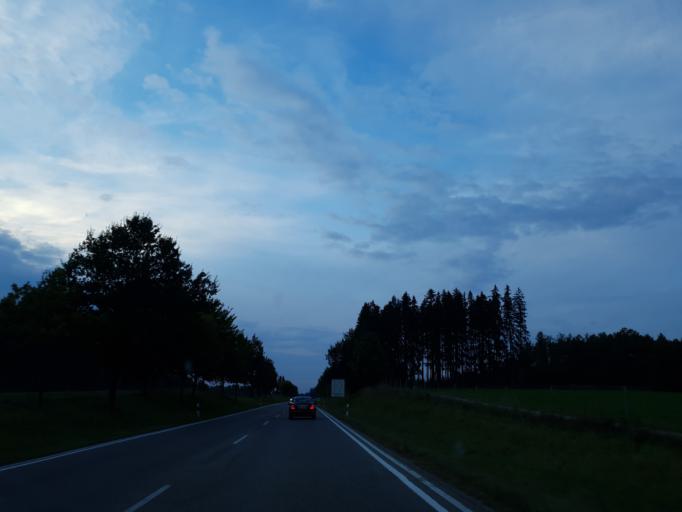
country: DE
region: Bavaria
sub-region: Swabia
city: Mauerstetten
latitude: 47.8547
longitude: 10.6627
